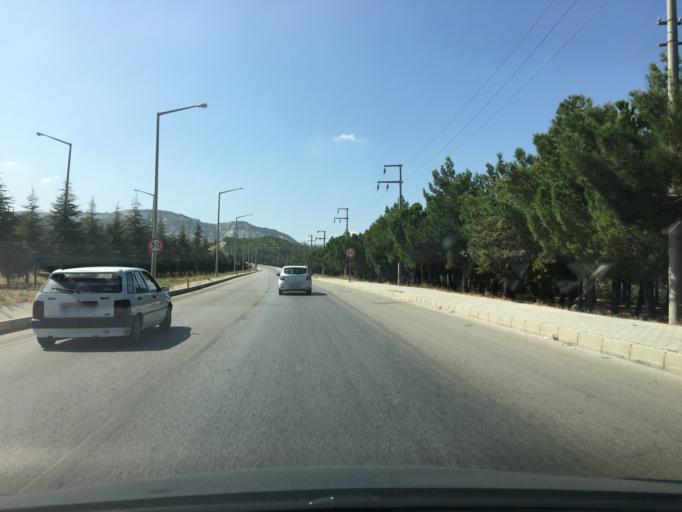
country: TR
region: Burdur
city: Burdur
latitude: 37.7249
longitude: 30.2996
